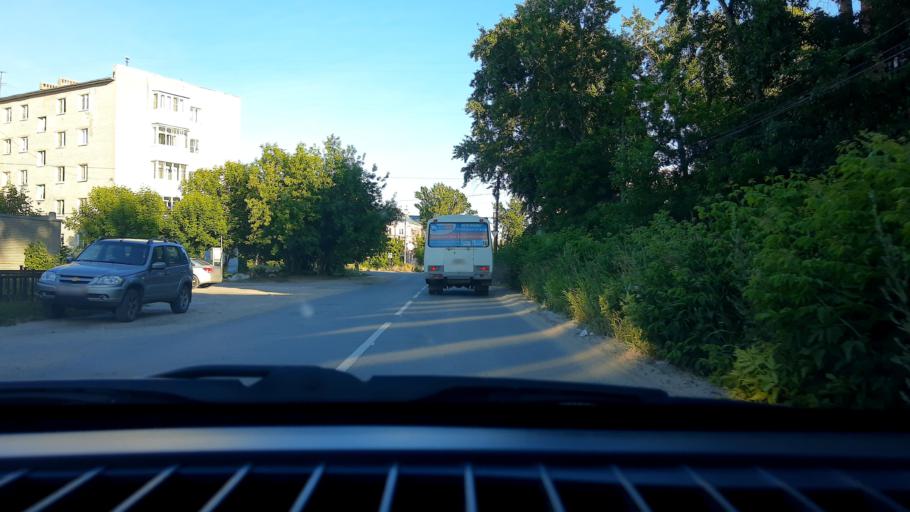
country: RU
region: Nizjnij Novgorod
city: Dzerzhinsk
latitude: 56.2408
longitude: 43.4881
